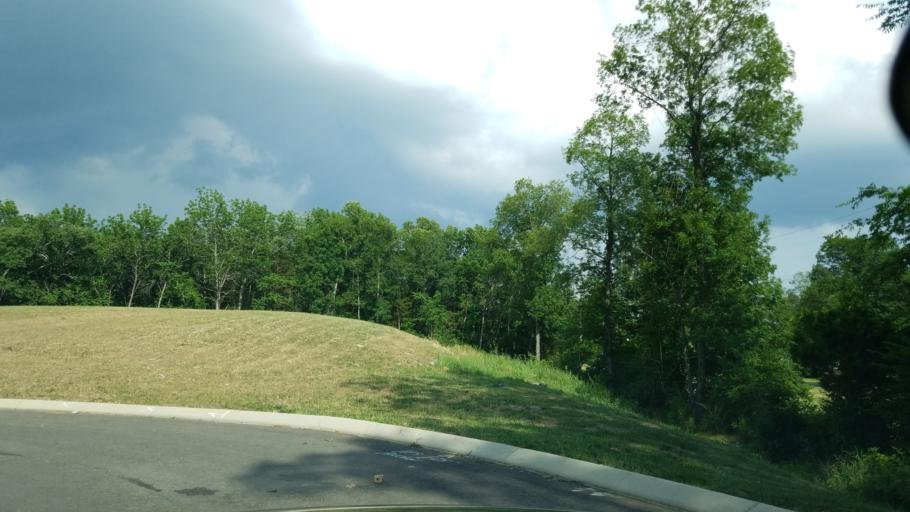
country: US
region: Tennessee
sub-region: Rutherford County
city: La Vergne
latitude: 36.0659
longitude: -86.5913
